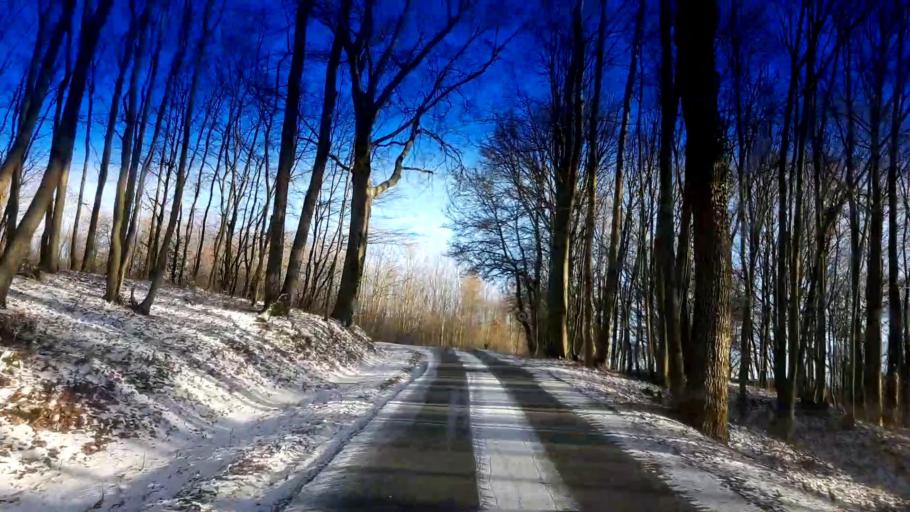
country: DE
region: Bavaria
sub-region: Upper Franconia
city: Buttenheim
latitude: 49.8350
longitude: 11.0851
